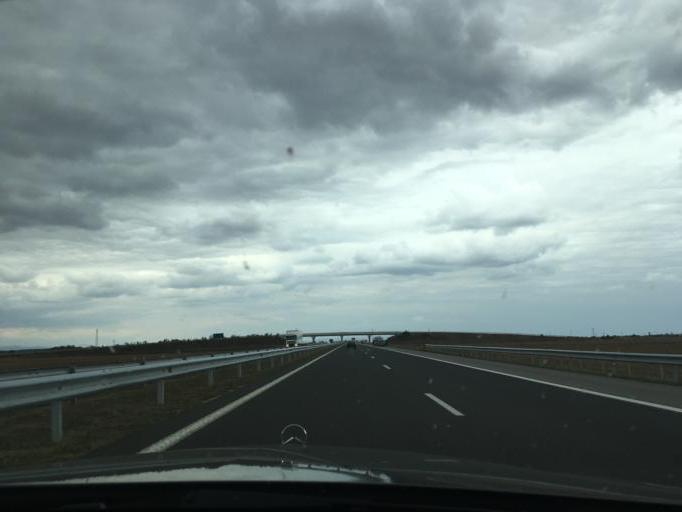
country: BG
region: Stara Zagora
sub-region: Obshtina Stara Zagora
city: Stara Zagora
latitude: 42.3664
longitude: 25.7844
